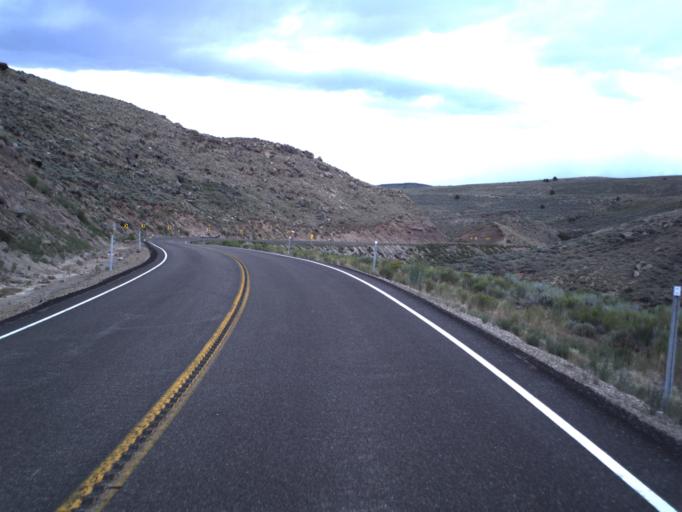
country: US
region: Utah
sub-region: Carbon County
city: Helper
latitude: 39.7906
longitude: -110.7886
